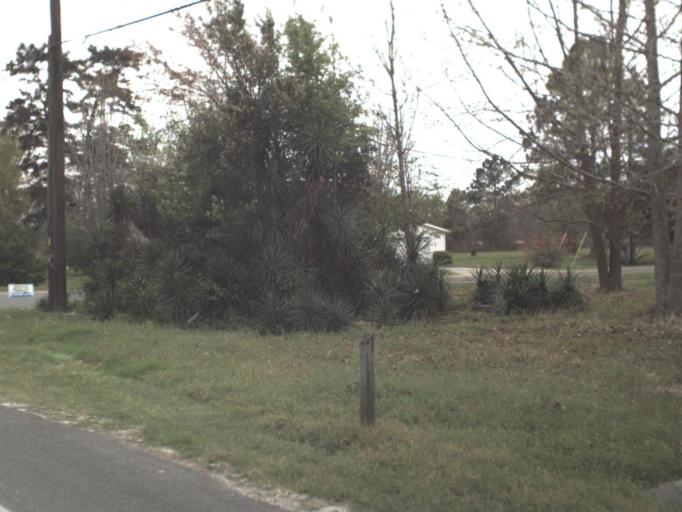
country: US
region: Florida
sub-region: Gulf County
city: Wewahitchka
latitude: 30.0978
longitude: -85.1990
